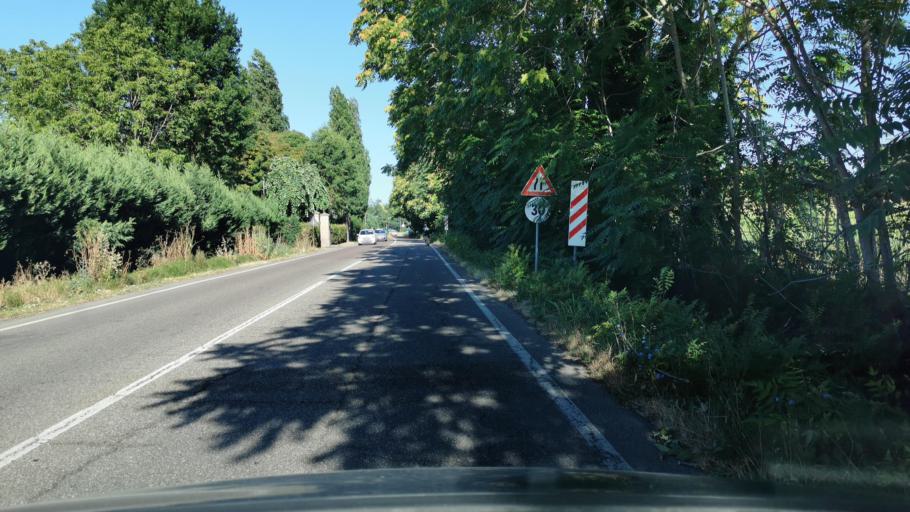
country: IT
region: Emilia-Romagna
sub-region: Provincia di Modena
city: Modena
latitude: 44.6194
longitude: 10.8989
